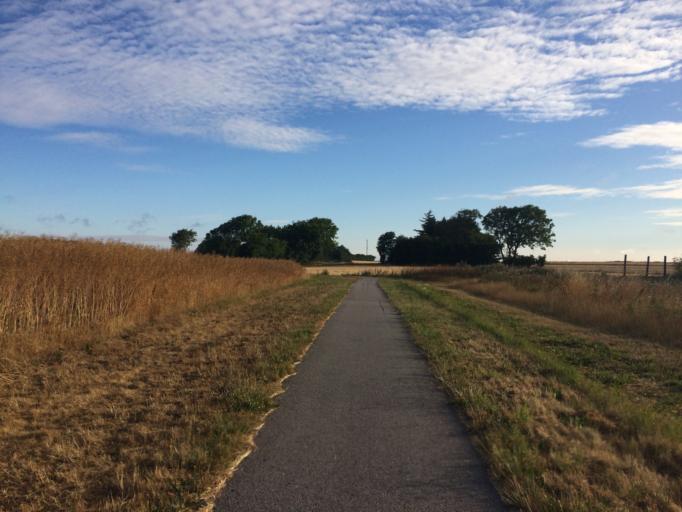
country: DK
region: Central Jutland
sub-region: Holstebro Kommune
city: Vinderup
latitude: 56.6031
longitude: 8.8660
